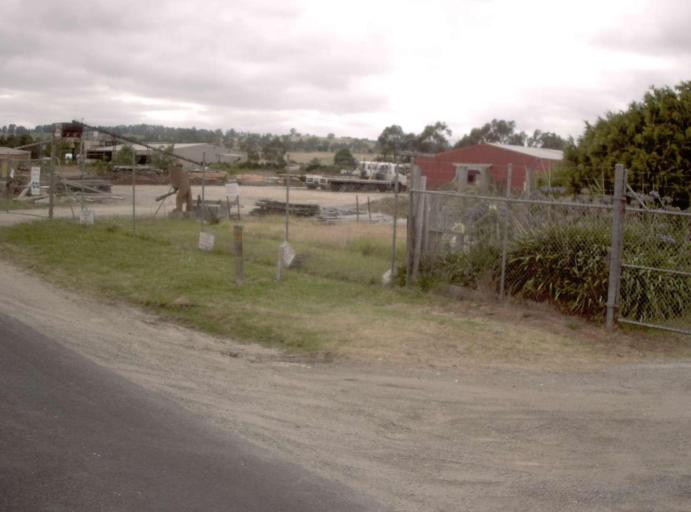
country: AU
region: Victoria
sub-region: Cardinia
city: Bunyip
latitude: -38.1078
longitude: 145.7784
